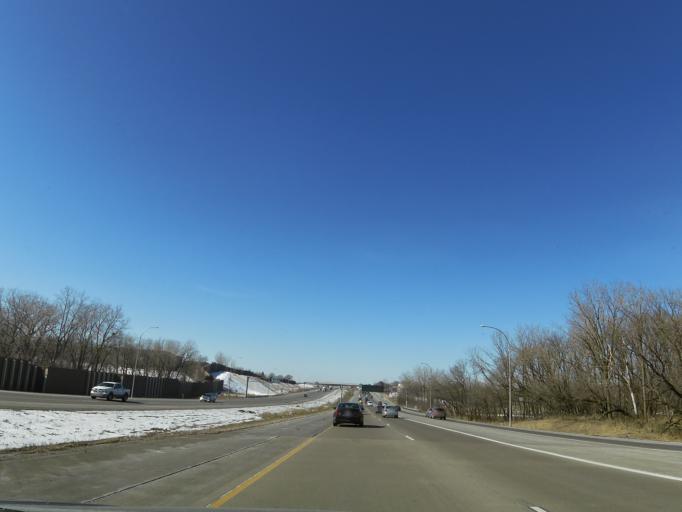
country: US
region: Minnesota
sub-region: Ramsey County
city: Vadnais Heights
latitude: 45.0377
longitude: -93.0465
